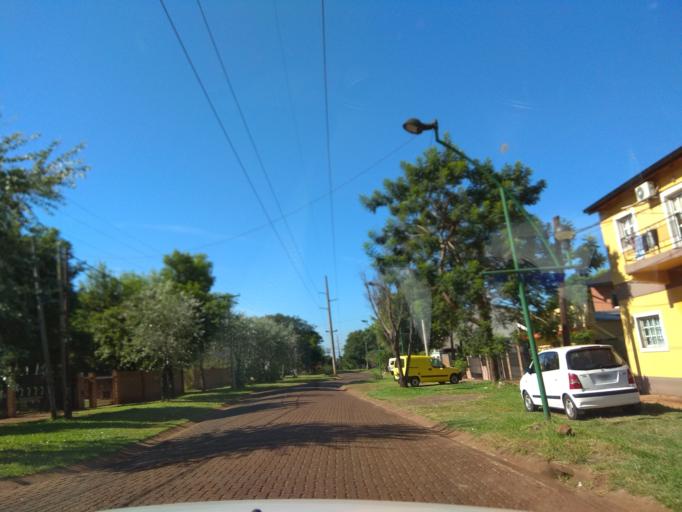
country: AR
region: Misiones
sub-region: Departamento de Capital
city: Posadas
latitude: -27.3938
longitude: -55.9165
